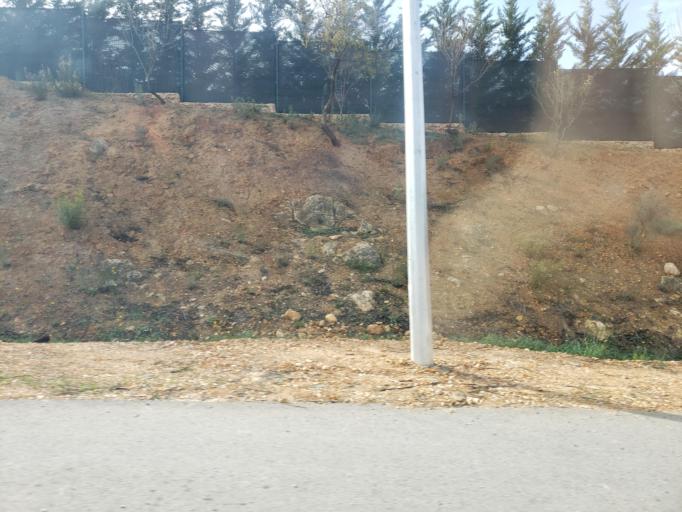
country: PT
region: Faro
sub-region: Portimao
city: Alvor
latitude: 37.1567
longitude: -8.5695
